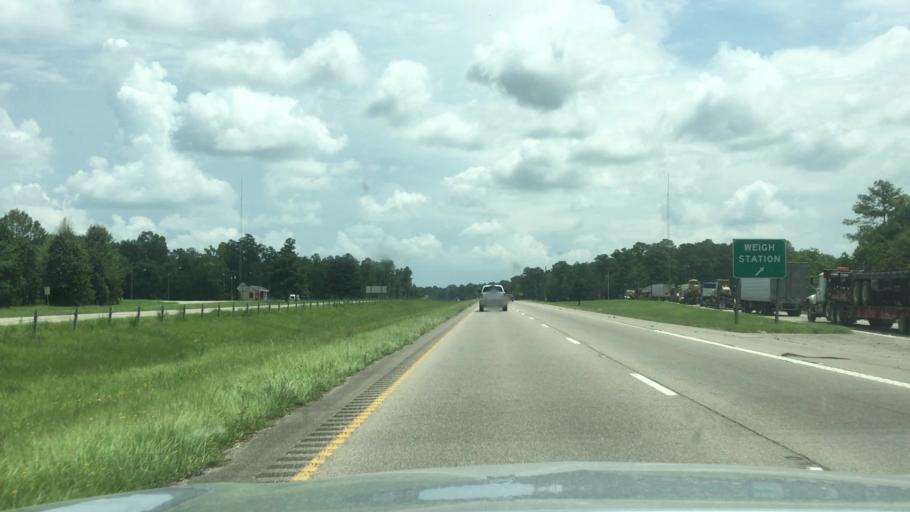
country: US
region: Mississippi
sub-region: Pearl River County
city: Nicholson
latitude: 30.4750
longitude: -89.6826
